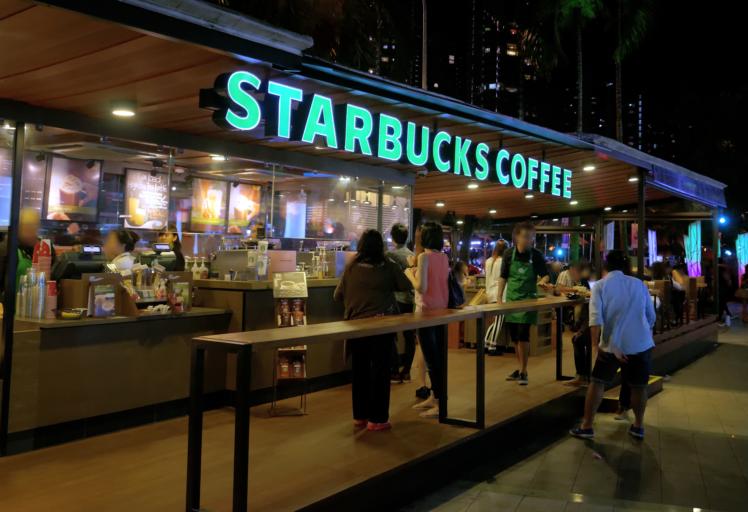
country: SG
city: Singapore
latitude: 1.3013
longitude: 103.8369
